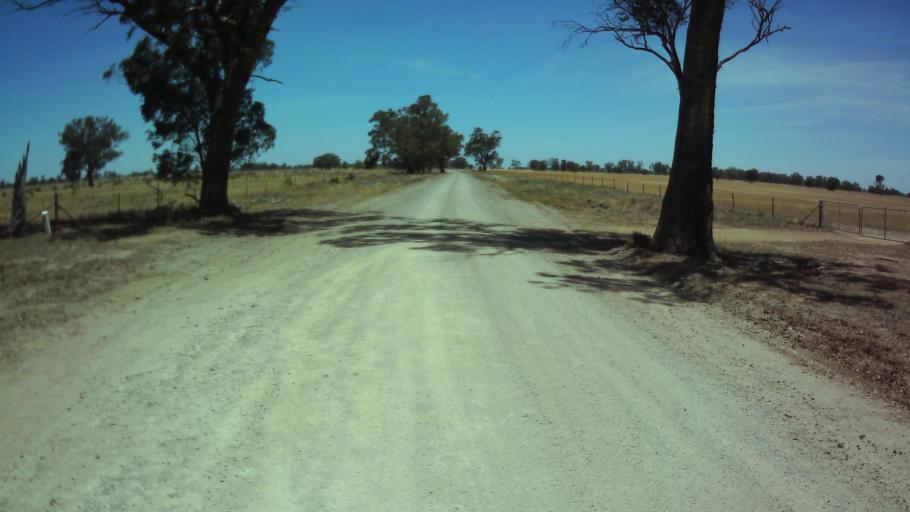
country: AU
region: New South Wales
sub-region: Weddin
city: Grenfell
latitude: -33.9991
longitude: 147.7371
